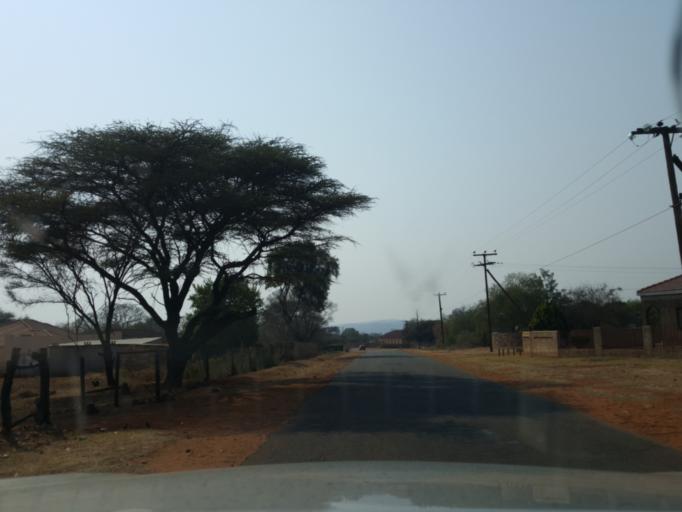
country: BW
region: South East
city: Lobatse
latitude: -25.2880
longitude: 25.9037
